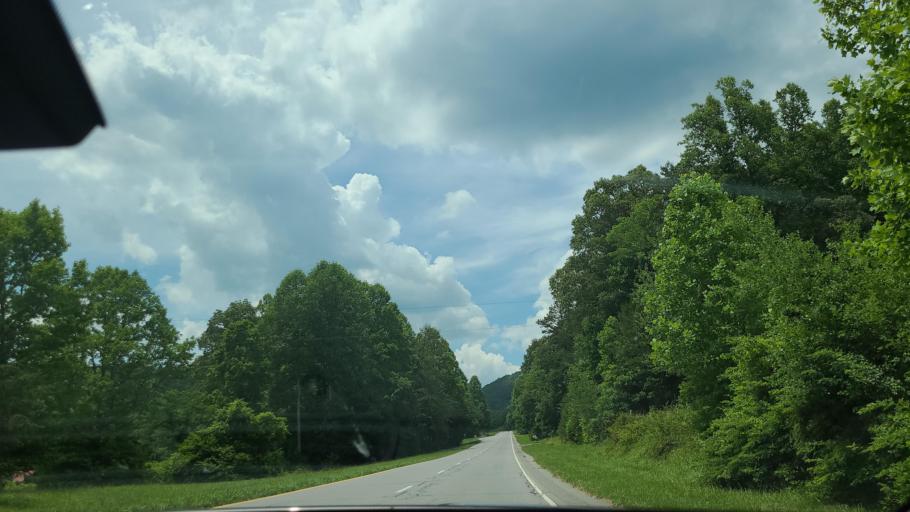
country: US
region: Georgia
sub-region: Fannin County
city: McCaysville
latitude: 35.0196
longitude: -84.2406
